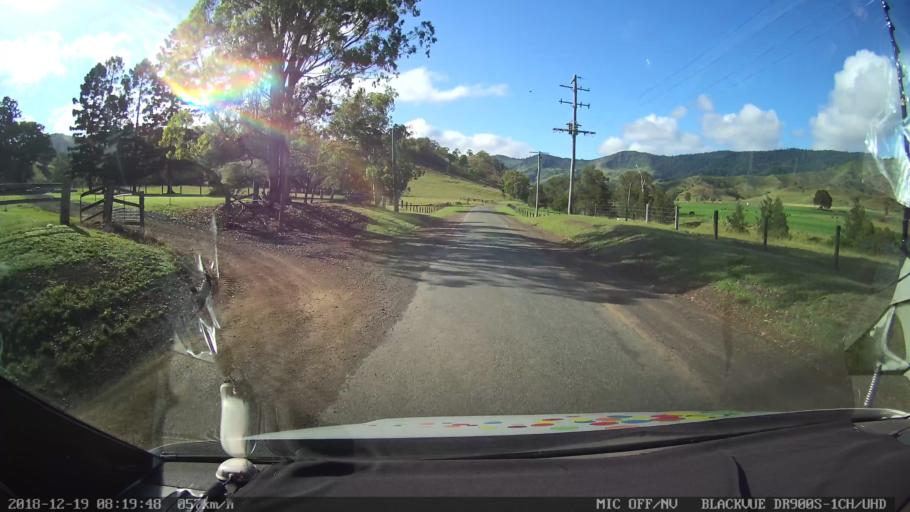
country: AU
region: New South Wales
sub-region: Kyogle
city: Kyogle
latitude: -28.2851
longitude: 152.9097
